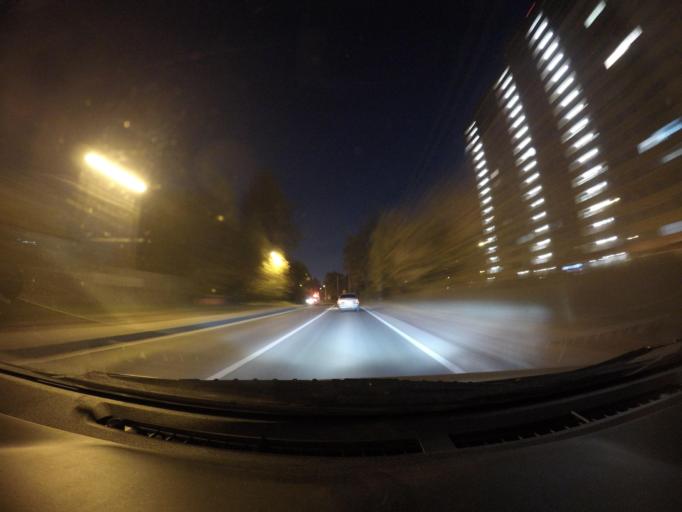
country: RU
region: Moskovskaya
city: Novopodrezkovo
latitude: 55.9221
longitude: 37.3750
